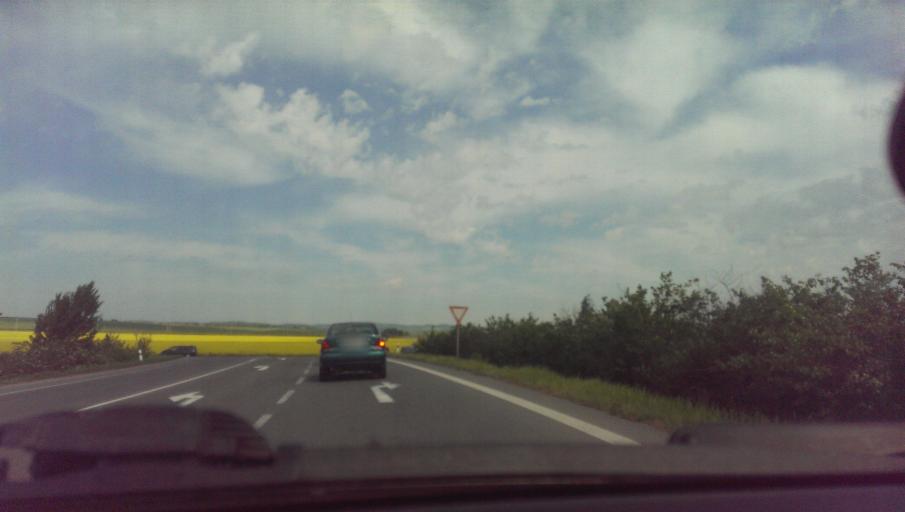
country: CZ
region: Zlin
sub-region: Okres Uherske Hradiste
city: Stare Mesto
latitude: 49.0891
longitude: 17.4489
